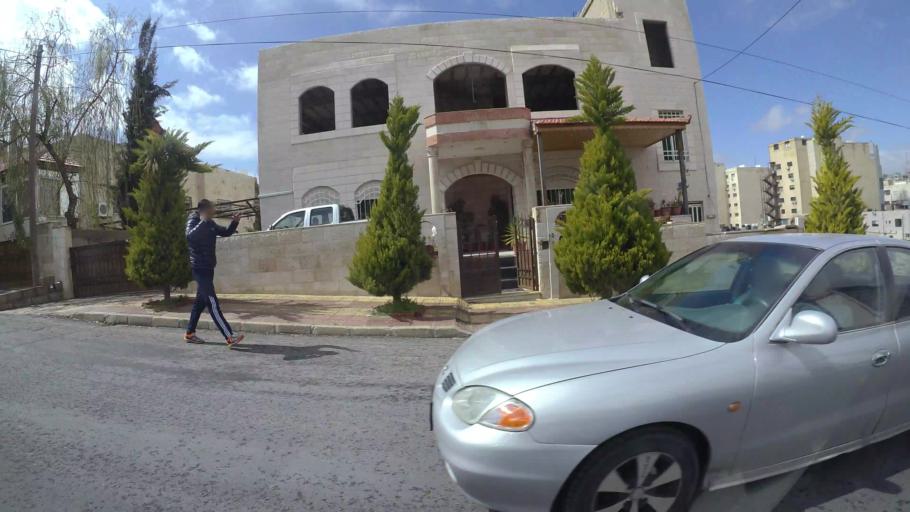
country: JO
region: Amman
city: Al Jubayhah
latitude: 31.9960
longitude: 35.8507
